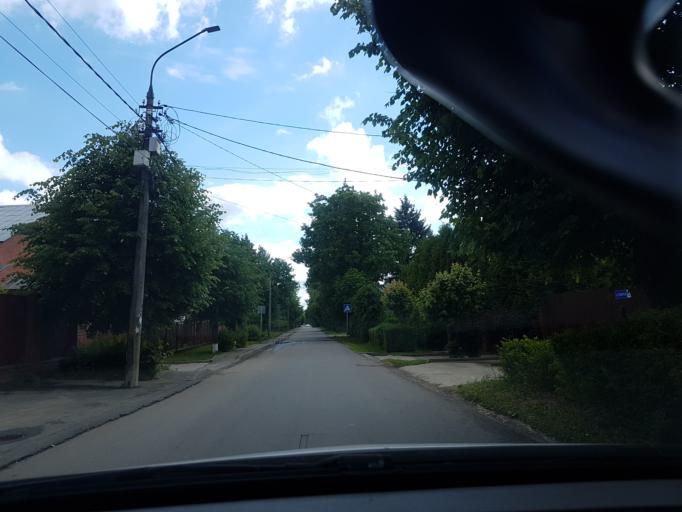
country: RU
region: Moskovskaya
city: Istra
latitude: 55.9185
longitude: 36.8756
